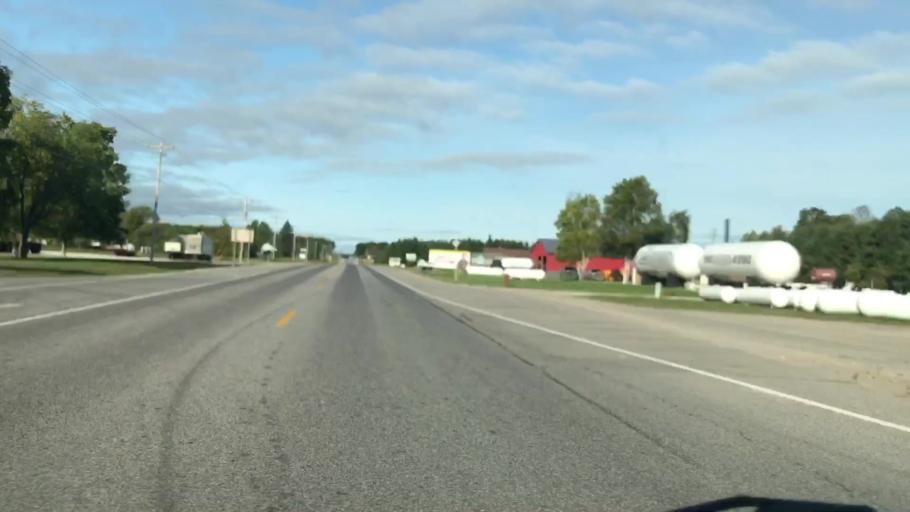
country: US
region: Michigan
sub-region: Luce County
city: Newberry
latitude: 46.3035
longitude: -85.4891
